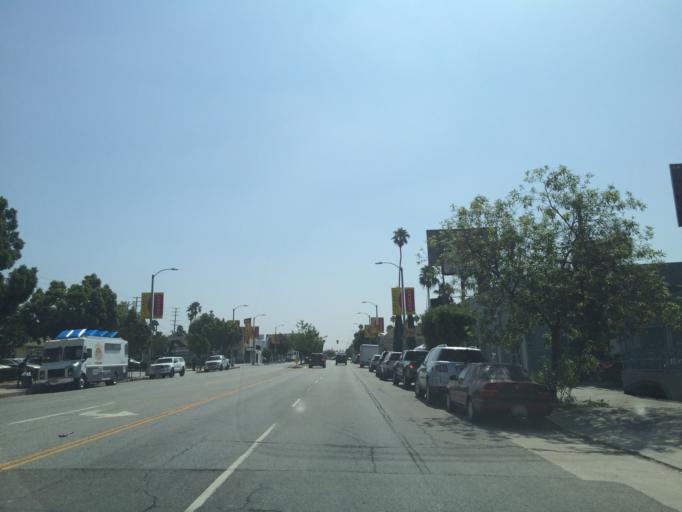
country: US
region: California
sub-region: Los Angeles County
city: West Hollywood
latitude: 34.0481
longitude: -118.3515
